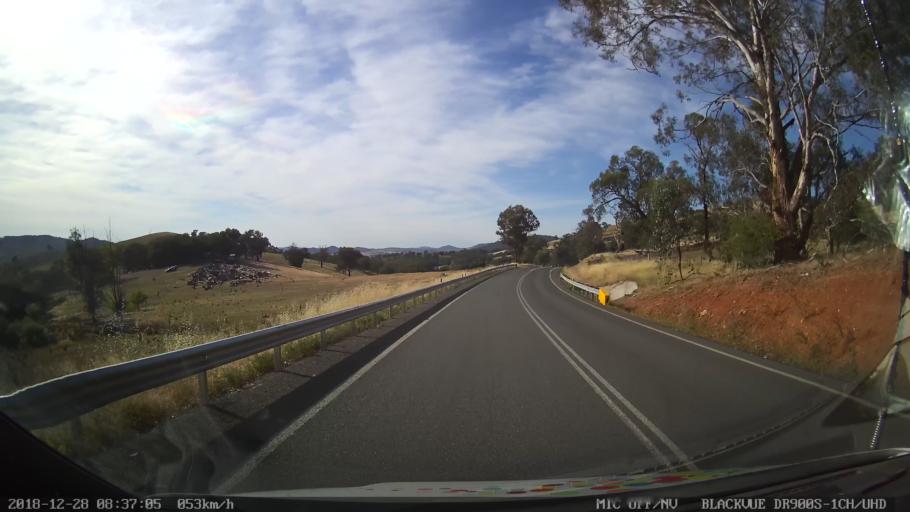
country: AU
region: New South Wales
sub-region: Blayney
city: Blayney
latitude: -33.9924
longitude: 149.3131
